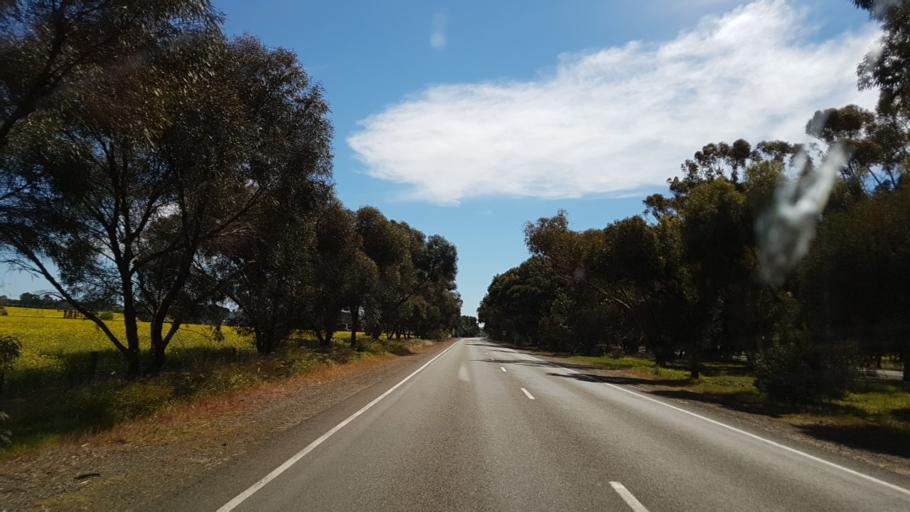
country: AU
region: South Australia
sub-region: Light
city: Kapunda
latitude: -34.1713
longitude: 138.7458
